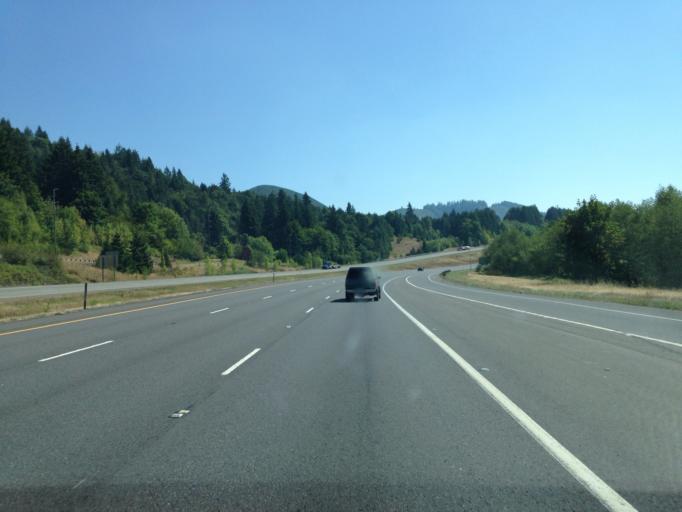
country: US
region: Washington
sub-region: Cowlitz County
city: Castle Rock
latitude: 46.2569
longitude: -122.8855
